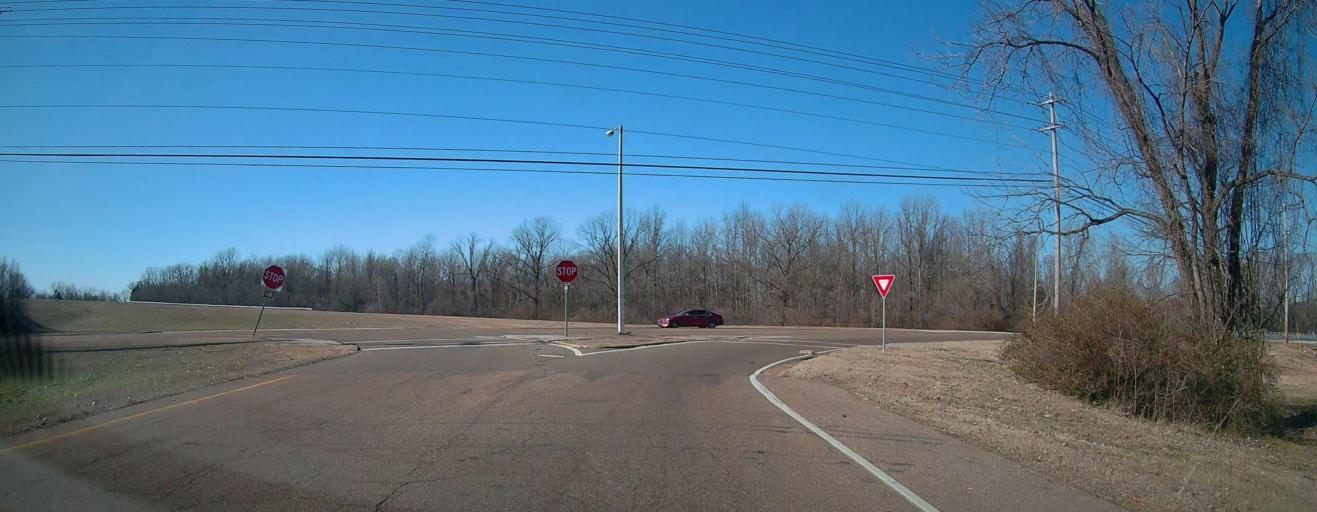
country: US
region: Tennessee
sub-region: Shelby County
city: Millington
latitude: 35.3313
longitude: -89.8977
